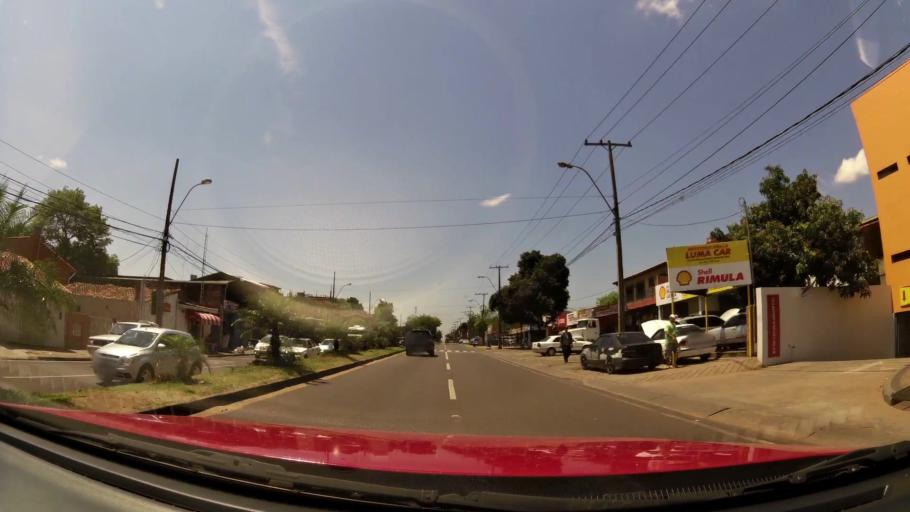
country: PY
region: Central
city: Lambare
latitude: -25.3336
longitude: -57.5775
